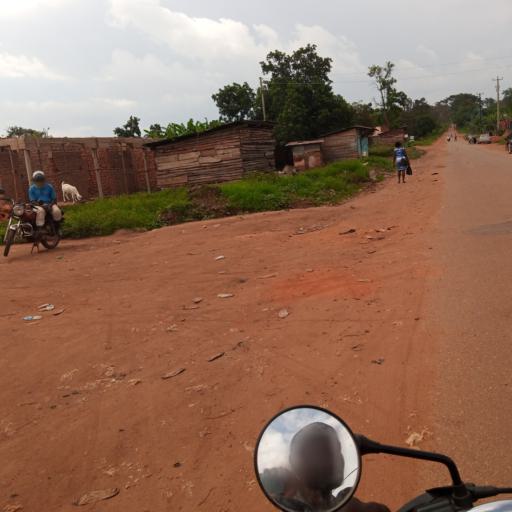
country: UG
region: Eastern Region
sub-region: Mbale District
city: Mbale
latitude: 1.0881
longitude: 34.1839
